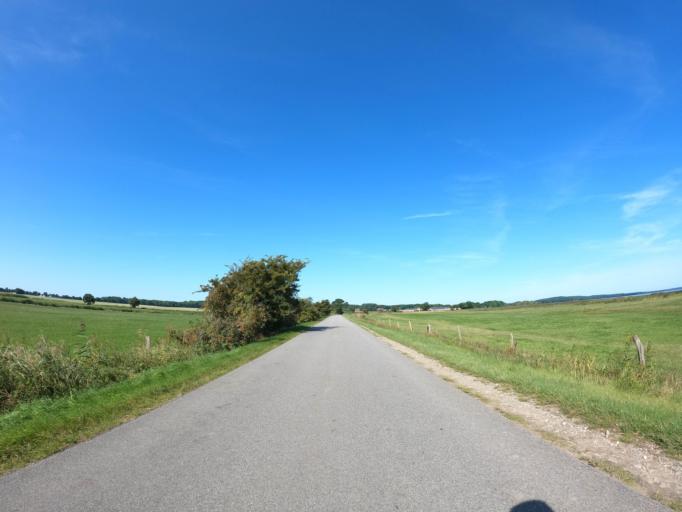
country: DE
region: Mecklenburg-Vorpommern
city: Prohn
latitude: 54.3940
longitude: 13.0256
